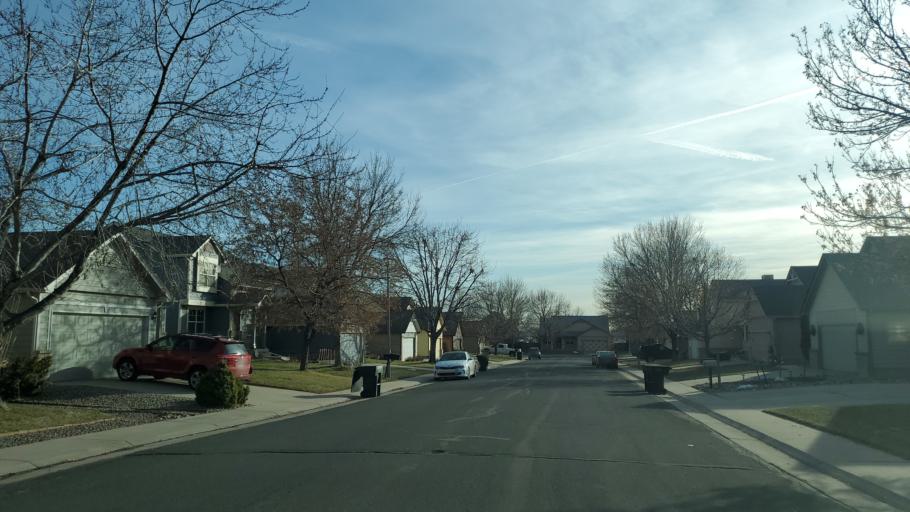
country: US
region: Colorado
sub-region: Adams County
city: Northglenn
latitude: 39.9065
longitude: -104.9566
